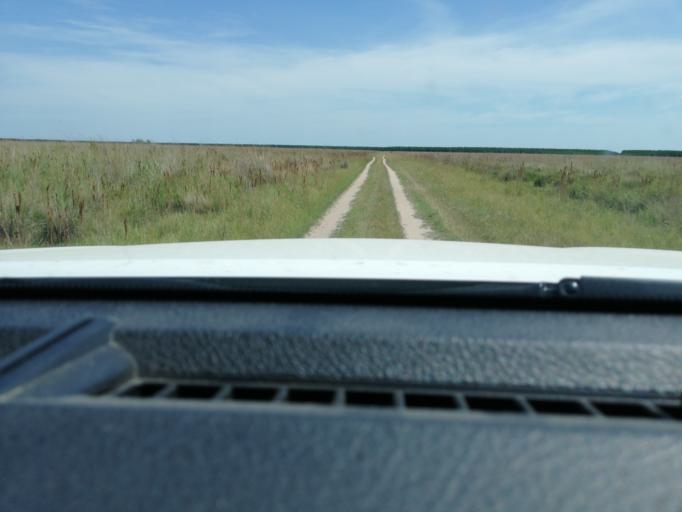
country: AR
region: Corrientes
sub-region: Departamento de San Miguel
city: San Miguel
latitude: -28.0528
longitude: -57.4553
